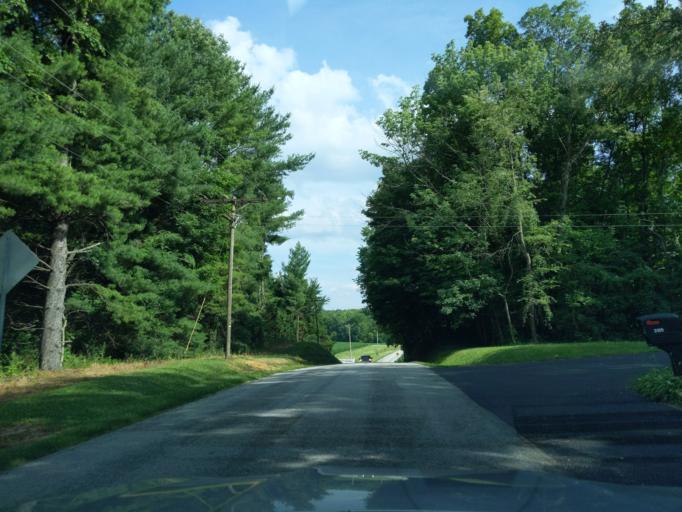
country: US
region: Indiana
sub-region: Decatur County
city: Greensburg
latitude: 39.2915
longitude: -85.4691
